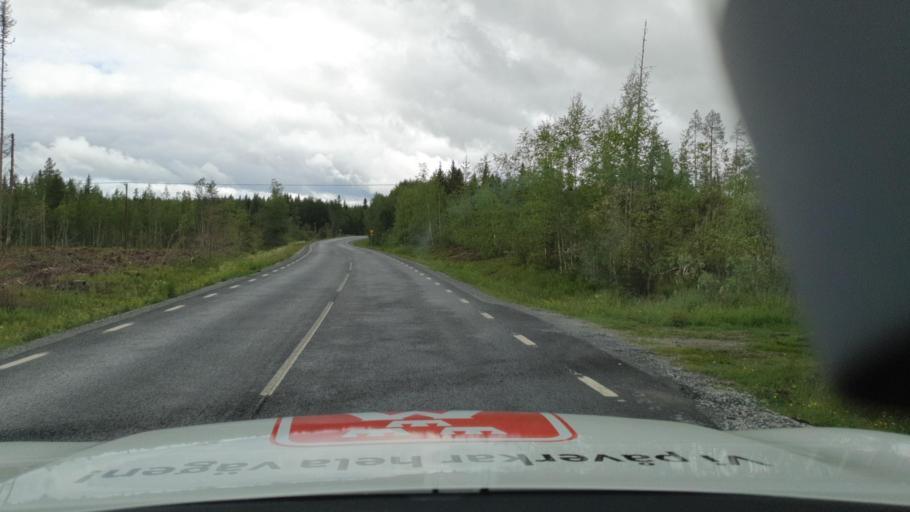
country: SE
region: Vaesterbotten
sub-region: Dorotea Kommun
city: Dorotea
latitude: 64.2466
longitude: 16.5330
